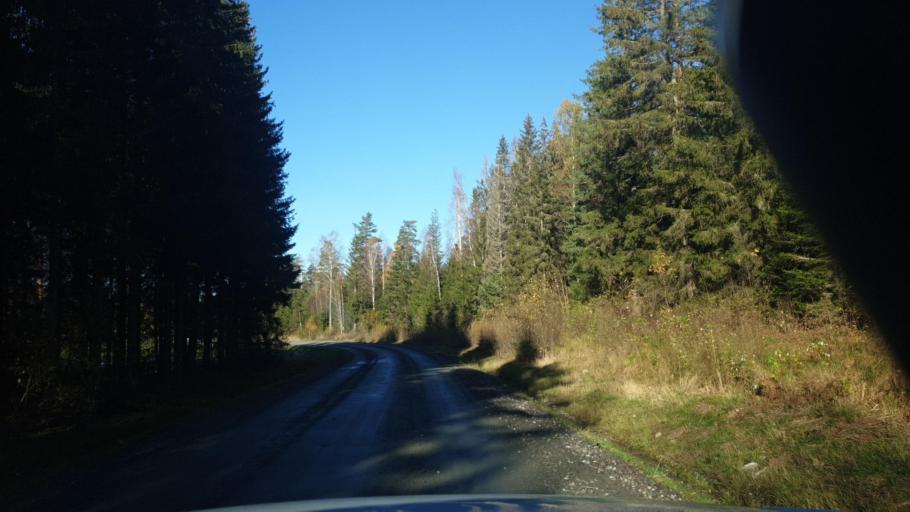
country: SE
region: Vaermland
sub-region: Karlstads Kommun
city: Edsvalla
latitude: 59.4490
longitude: 13.1538
